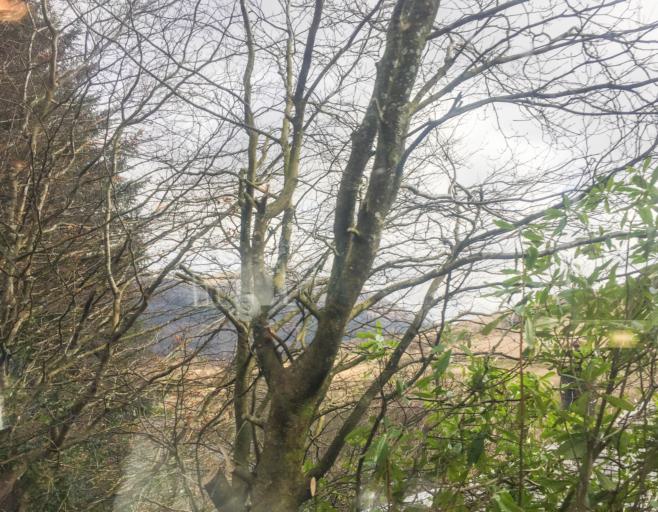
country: GB
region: Scotland
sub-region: Argyll and Bute
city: Garelochhead
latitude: 56.2033
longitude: -4.7230
